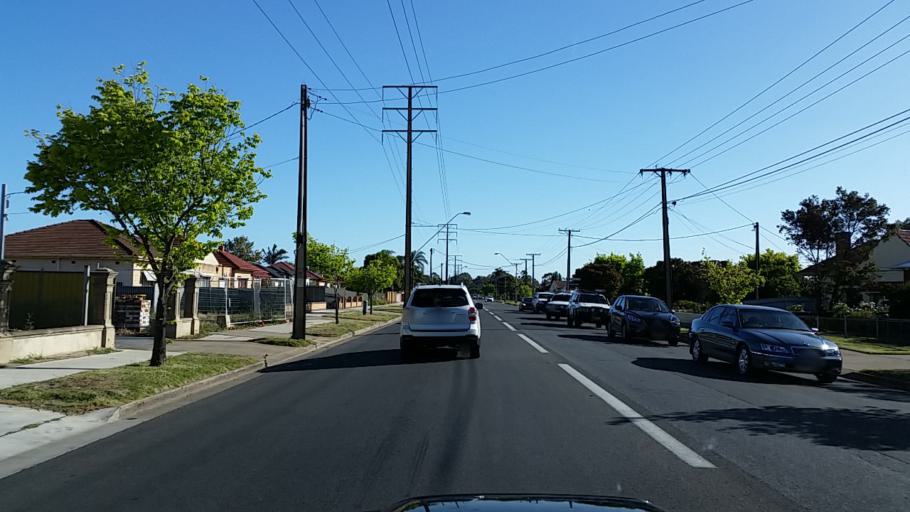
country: AU
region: South Australia
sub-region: Charles Sturt
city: Allenby Gardens
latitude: -34.9071
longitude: 138.5504
